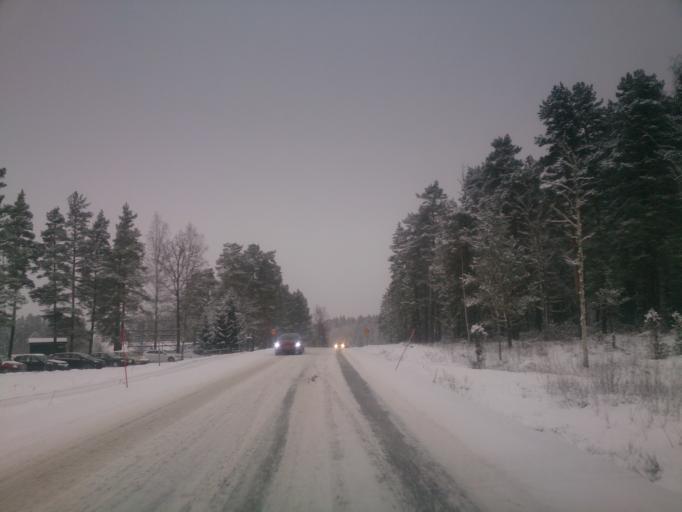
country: SE
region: OEstergoetland
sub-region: Finspangs Kommun
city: Finspang
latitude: 58.6893
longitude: 15.7505
